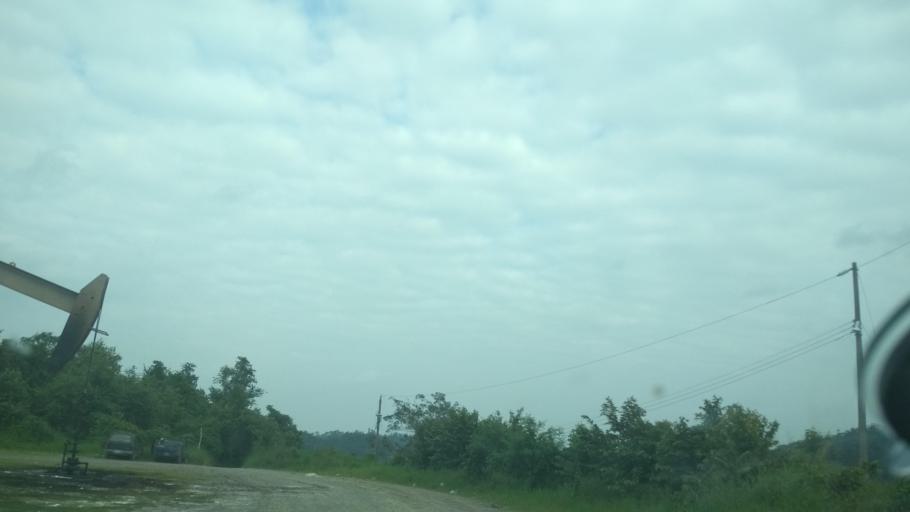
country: MX
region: Veracruz
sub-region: Poza Rica de Hidalgo
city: El Mollejon
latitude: 20.5236
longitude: -97.3774
